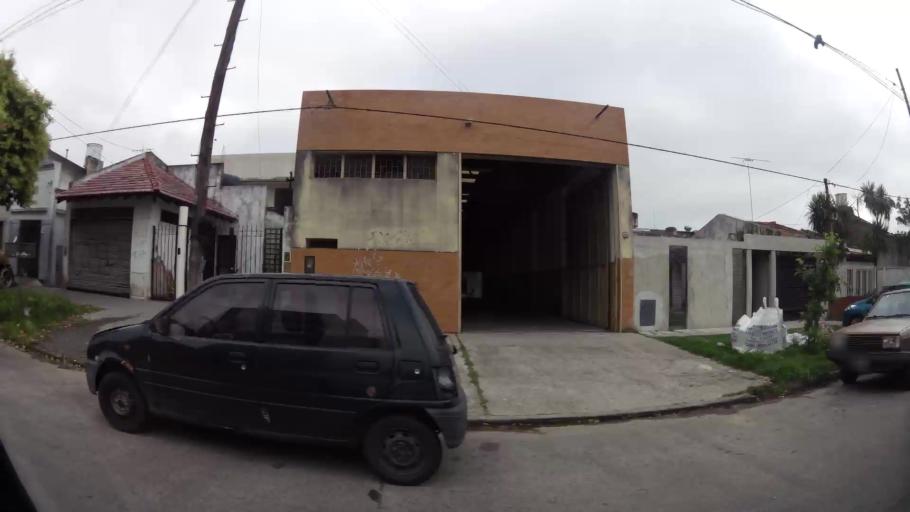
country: AR
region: Buenos Aires
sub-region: Partido de La Plata
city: La Plata
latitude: -34.9246
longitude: -57.9778
